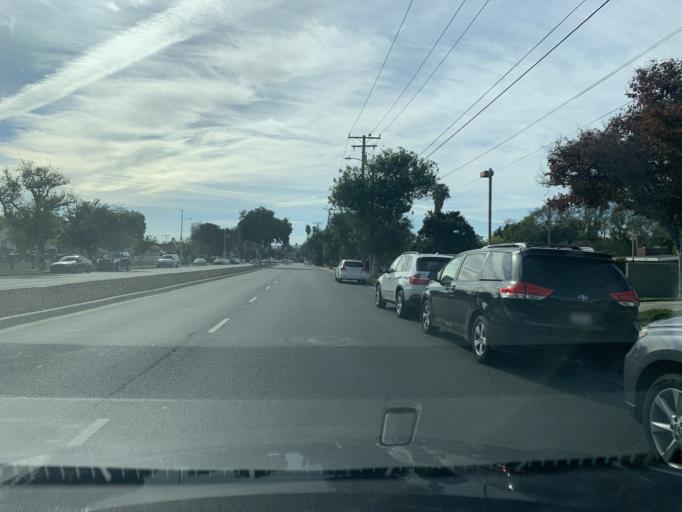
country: US
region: California
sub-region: Los Angeles County
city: West Covina
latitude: 34.0775
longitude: -117.9352
